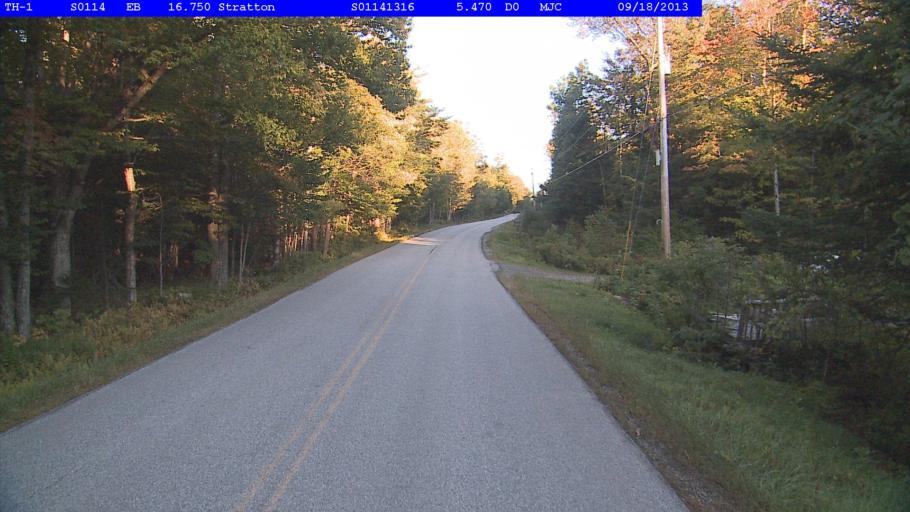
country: US
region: Vermont
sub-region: Windham County
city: Dover
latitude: 43.0408
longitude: -72.9063
